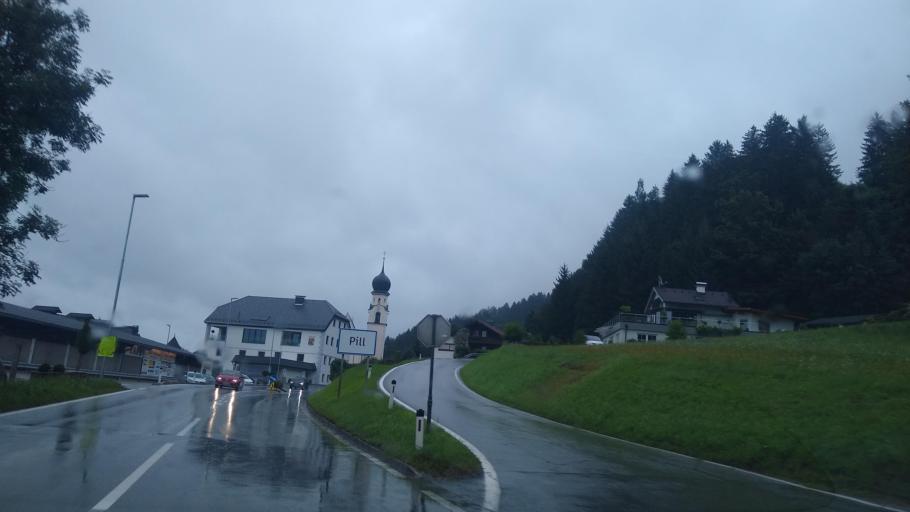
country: AT
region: Tyrol
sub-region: Politischer Bezirk Schwaz
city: Pill
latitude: 47.3192
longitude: 11.6794
